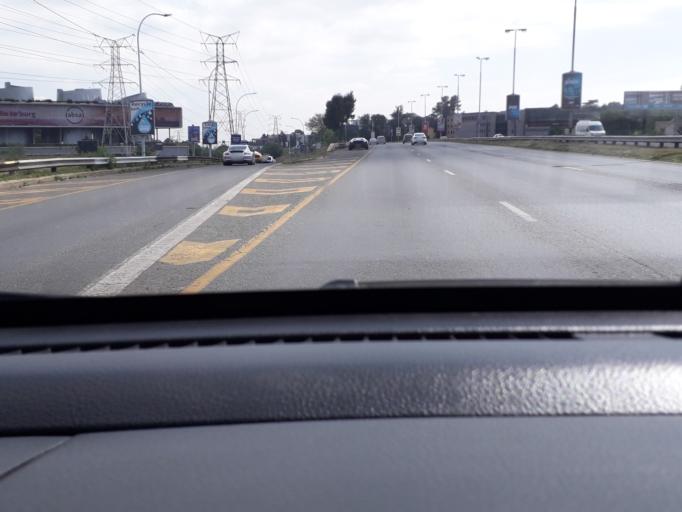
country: ZA
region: Gauteng
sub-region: City of Johannesburg Metropolitan Municipality
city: Johannesburg
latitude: -26.1312
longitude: 28.0710
